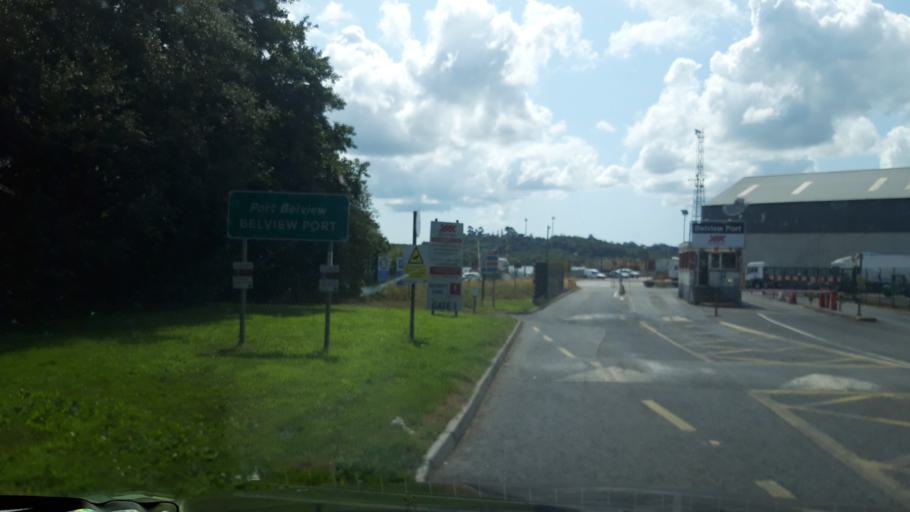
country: IE
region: Munster
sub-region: Waterford
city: Waterford
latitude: 52.2650
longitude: -7.0371
